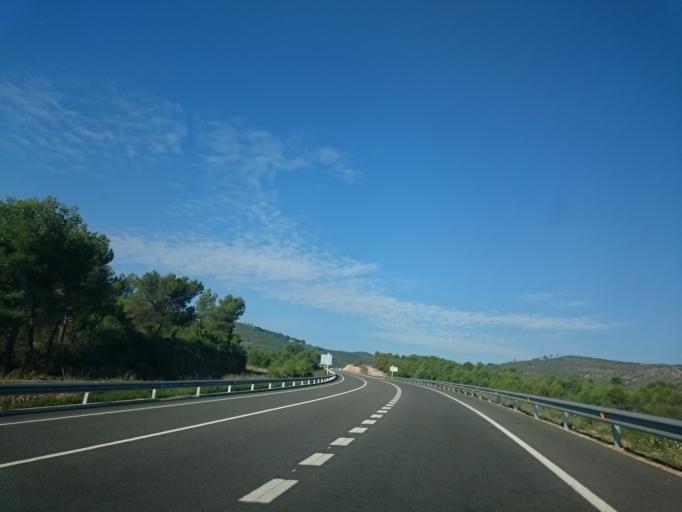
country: ES
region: Catalonia
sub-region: Provincia de Tarragona
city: la Bisbal del Penedes
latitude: 41.2732
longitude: 1.4562
